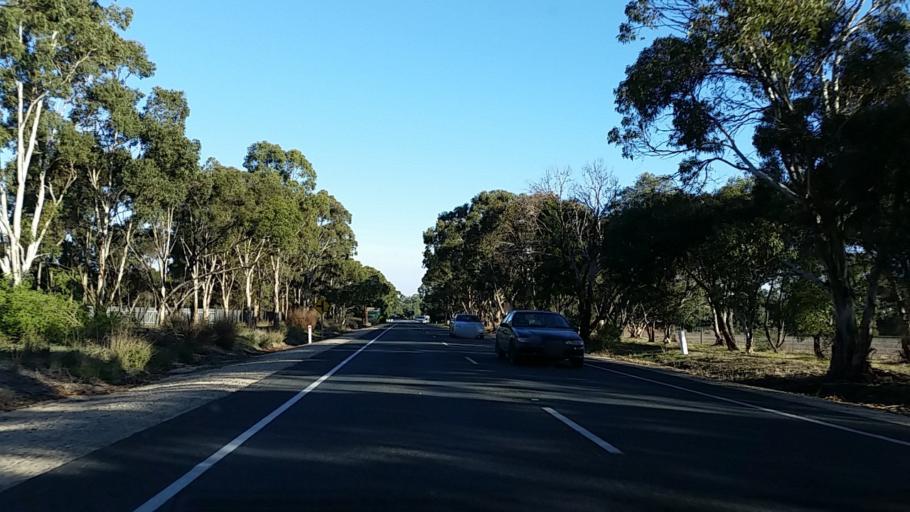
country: AU
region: South Australia
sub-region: Alexandrina
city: Strathalbyn
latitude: -35.2392
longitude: 138.8943
